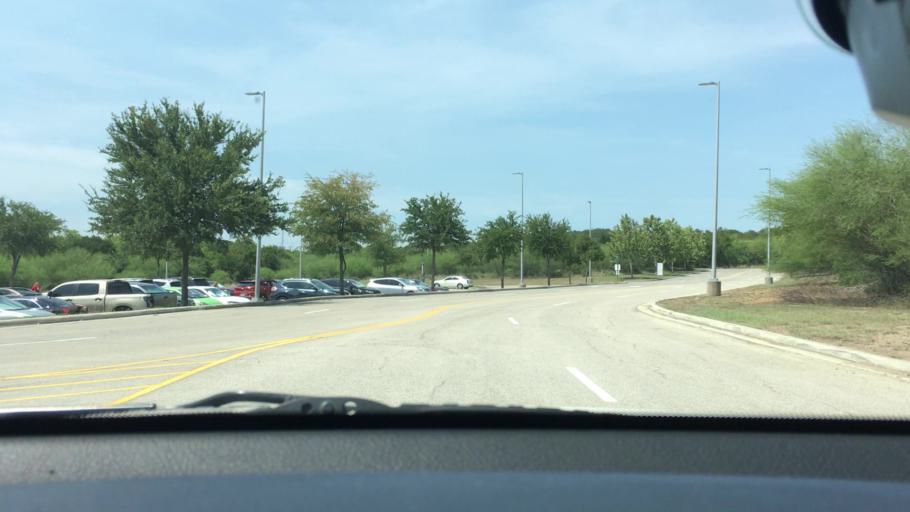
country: US
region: Texas
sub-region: Bexar County
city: Live Oak
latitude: 29.5491
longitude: -98.3254
